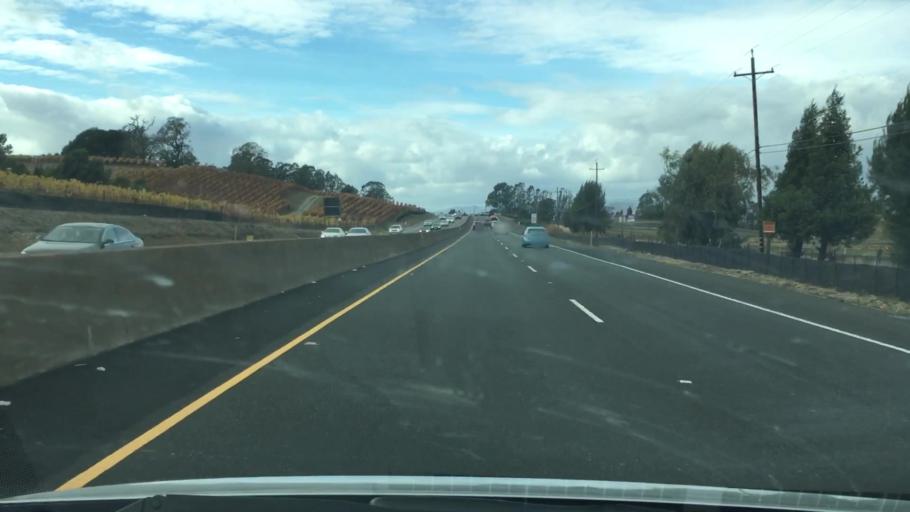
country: US
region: California
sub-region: Napa County
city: American Canyon
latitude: 38.2224
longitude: -122.2477
